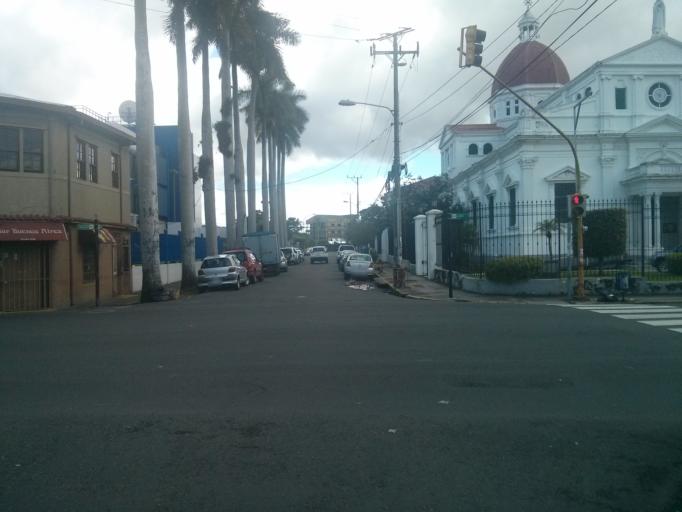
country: CR
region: San Jose
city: Calle Blancos
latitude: 9.9367
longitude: -84.0670
